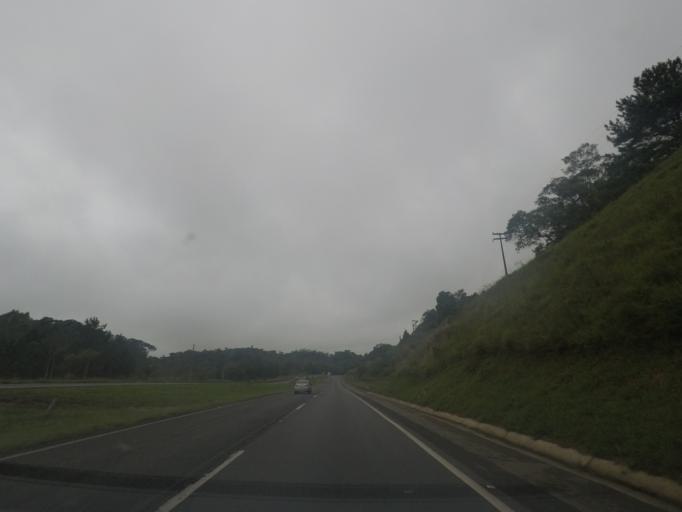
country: BR
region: Parana
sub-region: Antonina
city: Antonina
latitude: -25.0694
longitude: -48.5843
